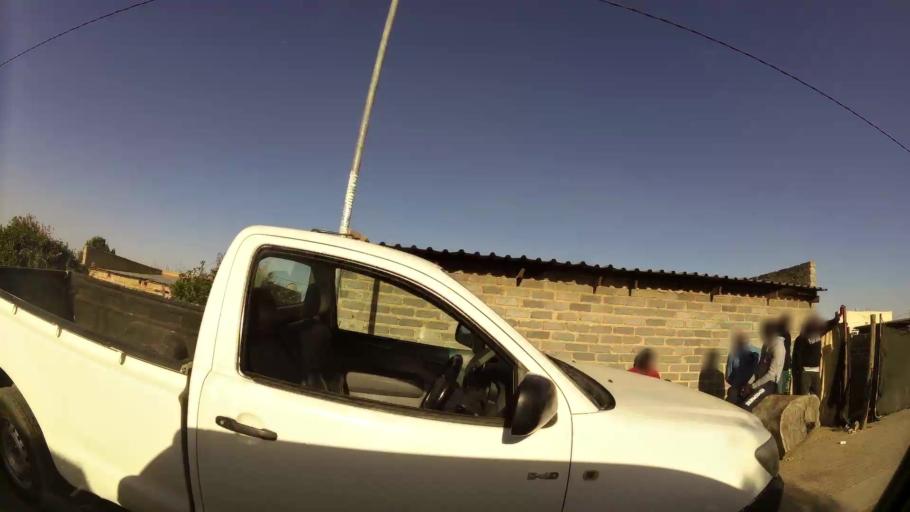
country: ZA
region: Gauteng
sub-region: City of Johannesburg Metropolitan Municipality
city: Diepsloot
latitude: -25.9303
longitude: 28.0062
